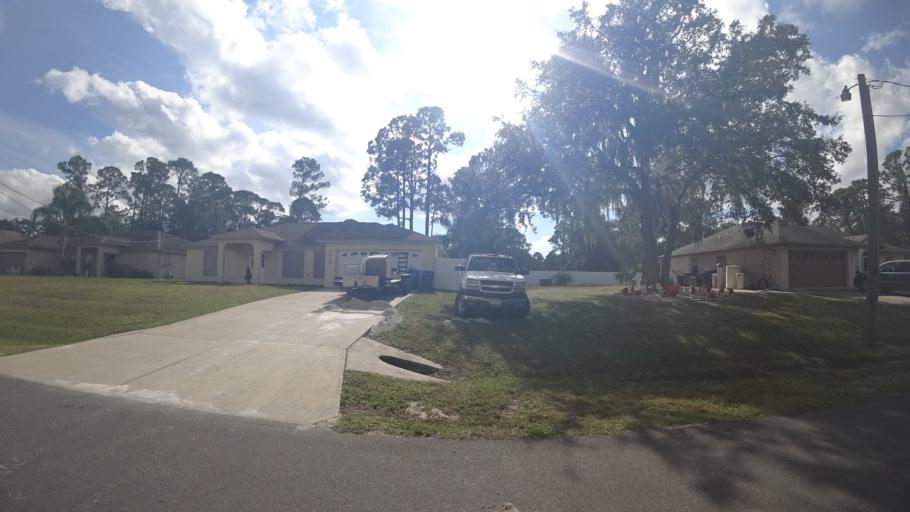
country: US
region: Florida
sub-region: Charlotte County
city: Port Charlotte
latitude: 27.0364
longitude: -82.1355
